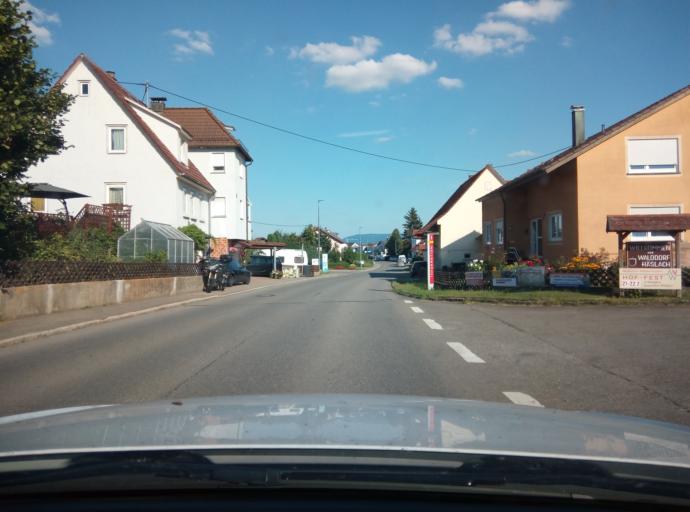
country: DE
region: Baden-Wuerttemberg
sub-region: Tuebingen Region
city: Pliezhausen
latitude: 48.5907
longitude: 9.1718
